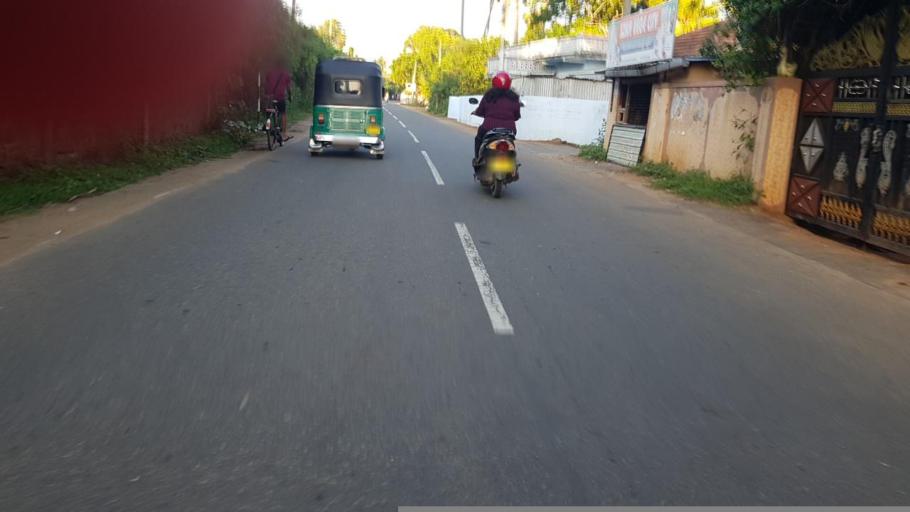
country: LK
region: Northern Province
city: Jaffna
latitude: 9.7315
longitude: 79.9505
